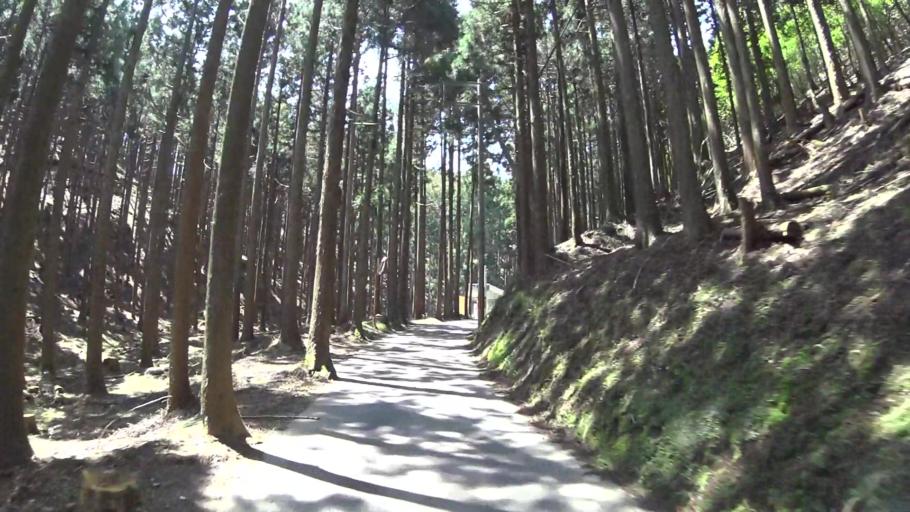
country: JP
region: Shiga Prefecture
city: Kitahama
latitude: 35.1573
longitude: 135.8010
